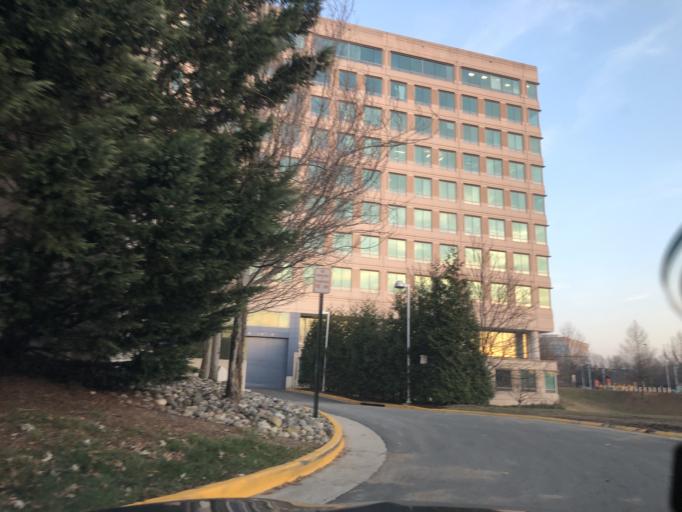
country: US
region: Virginia
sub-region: Fairfax County
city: Reston
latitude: 38.9560
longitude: -77.3586
